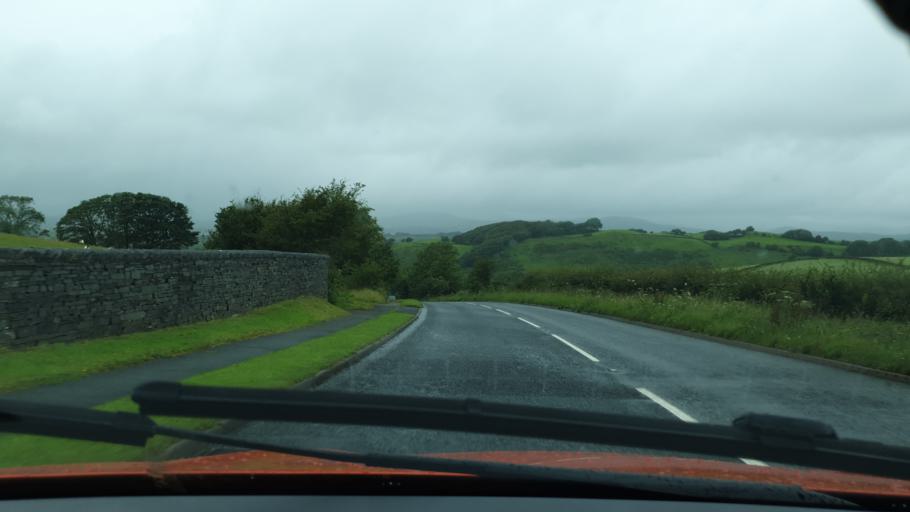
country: GB
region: England
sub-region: Cumbria
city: Askam in Furness
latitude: 54.2547
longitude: -3.1634
